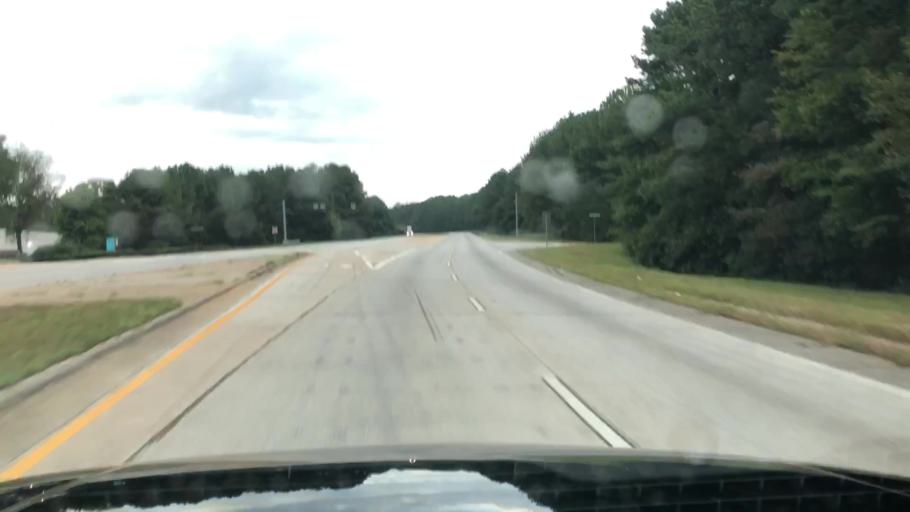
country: US
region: Georgia
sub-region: Cobb County
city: Mableton
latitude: 33.7194
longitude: -84.5758
